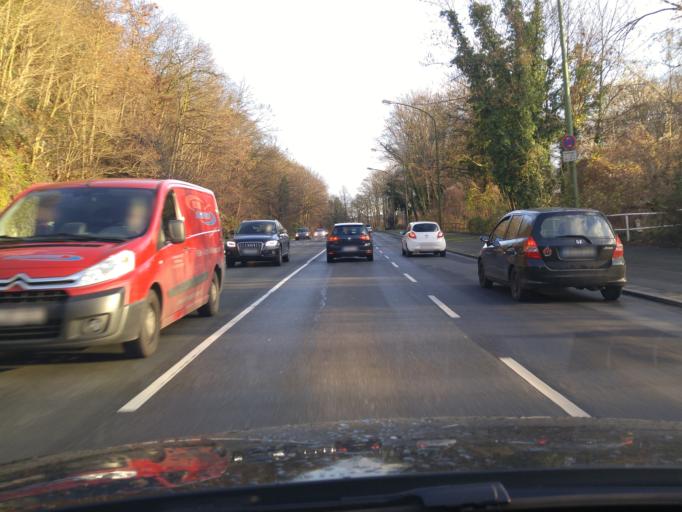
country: DE
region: North Rhine-Westphalia
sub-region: Regierungsbezirk Dusseldorf
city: Essen
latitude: 51.4395
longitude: 7.0612
